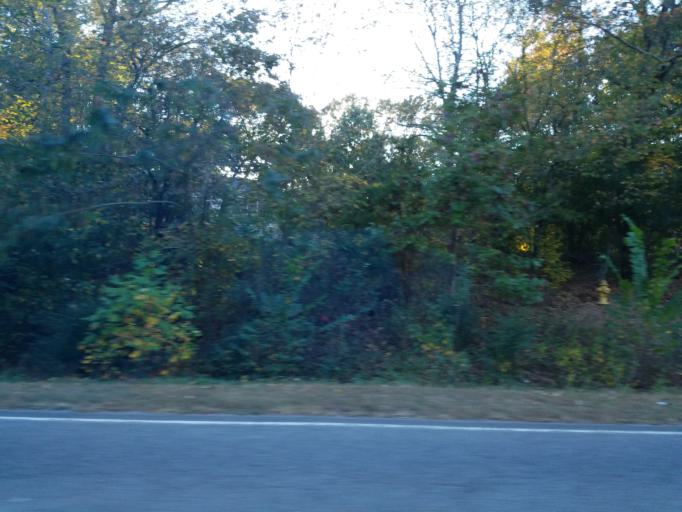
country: US
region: Georgia
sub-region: Bartow County
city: Adairsville
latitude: 34.3422
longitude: -84.9371
